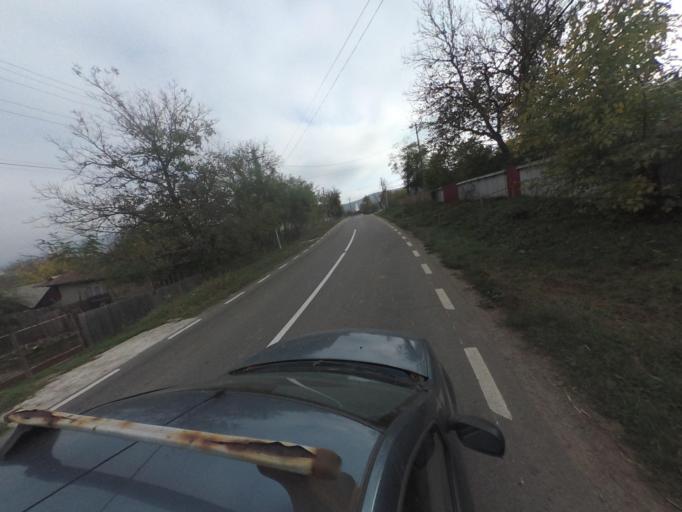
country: RO
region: Vaslui
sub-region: Comuna Bacesti
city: Bacesti
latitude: 46.8279
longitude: 27.2416
